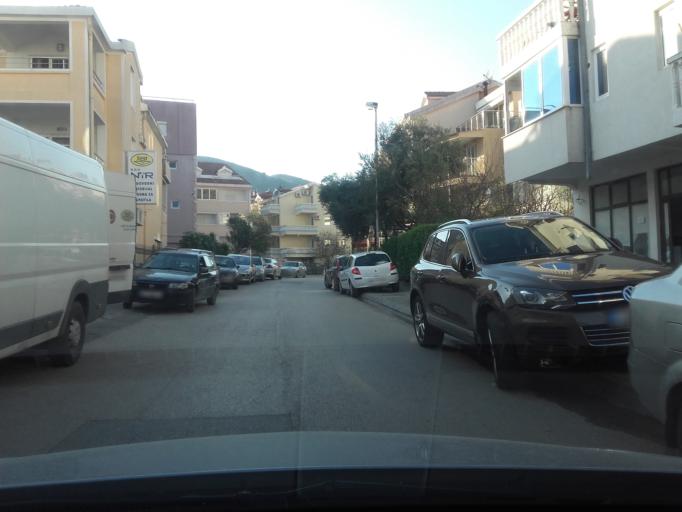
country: ME
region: Budva
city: Budva
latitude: 42.2904
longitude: 18.8480
